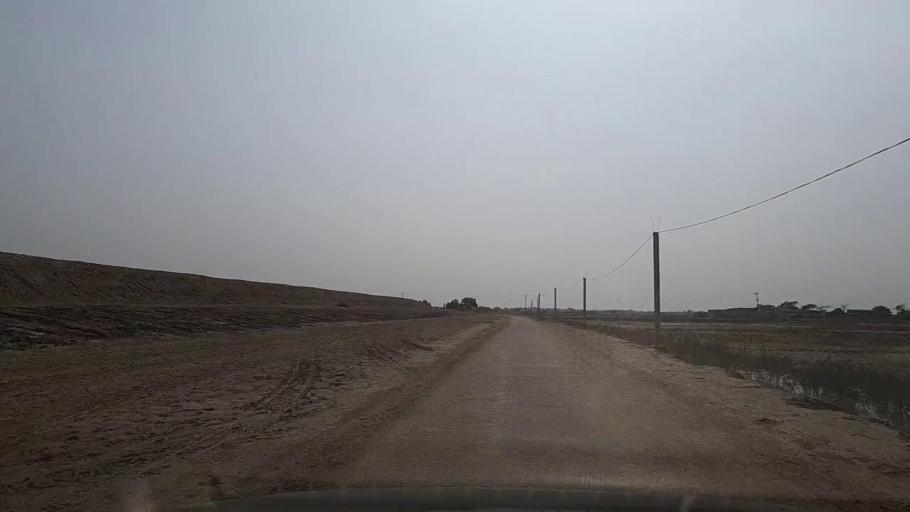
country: PK
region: Sindh
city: Thatta
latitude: 24.5651
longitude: 67.9132
